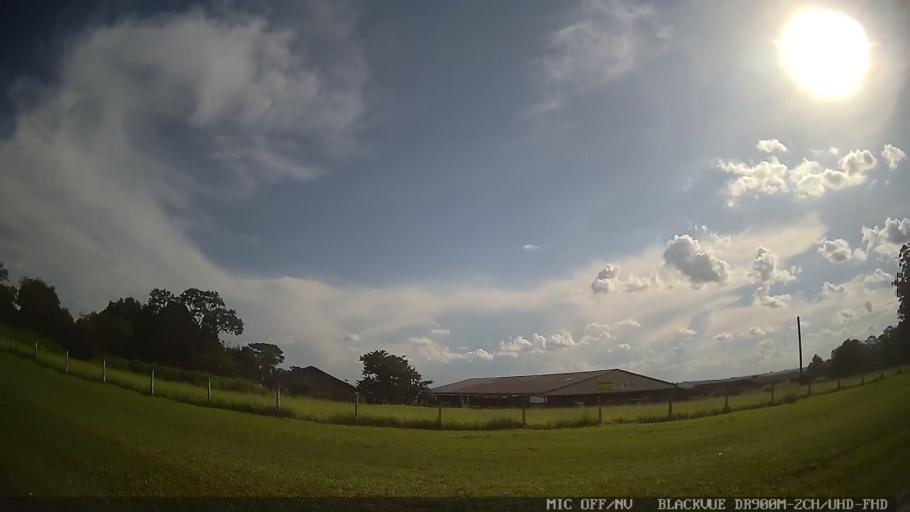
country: BR
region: Sao Paulo
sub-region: Laranjal Paulista
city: Laranjal Paulista
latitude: -23.0784
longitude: -47.7970
